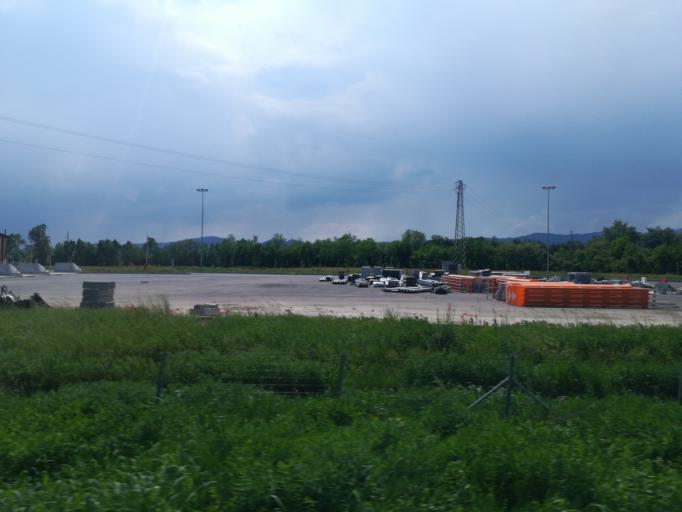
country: IT
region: Veneto
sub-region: Provincia di Vicenza
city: Novoledo
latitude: 45.6649
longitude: 11.5159
